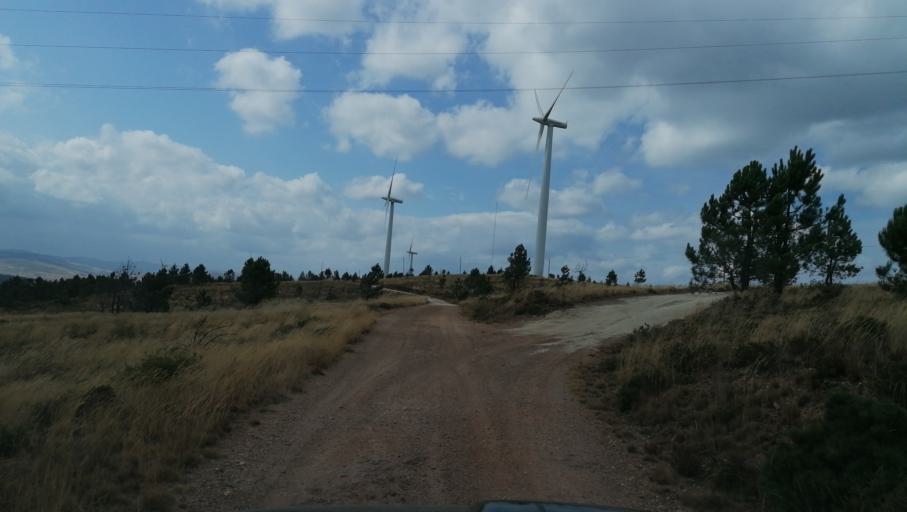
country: PT
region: Vila Real
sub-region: Vila Pouca de Aguiar
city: Vila Pouca de Aguiar
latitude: 41.5375
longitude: -7.7123
